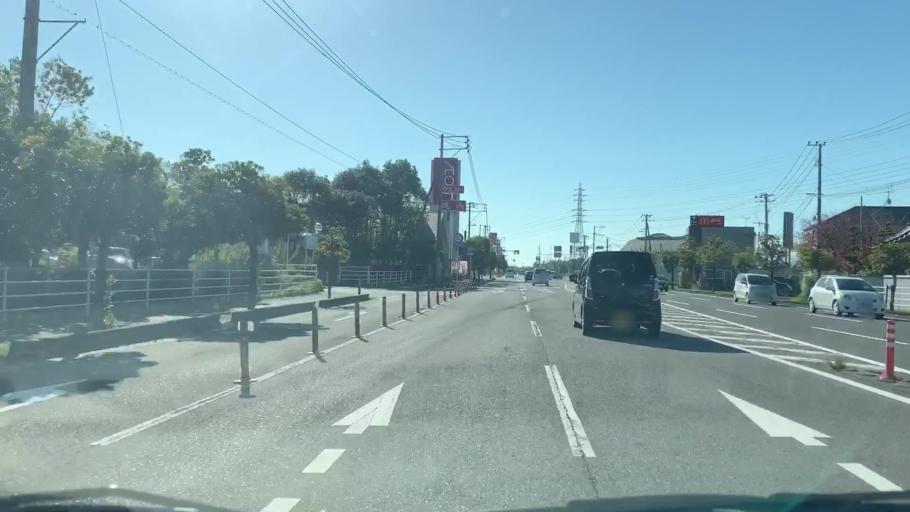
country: JP
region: Saga Prefecture
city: Saga-shi
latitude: 33.3042
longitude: 130.2787
